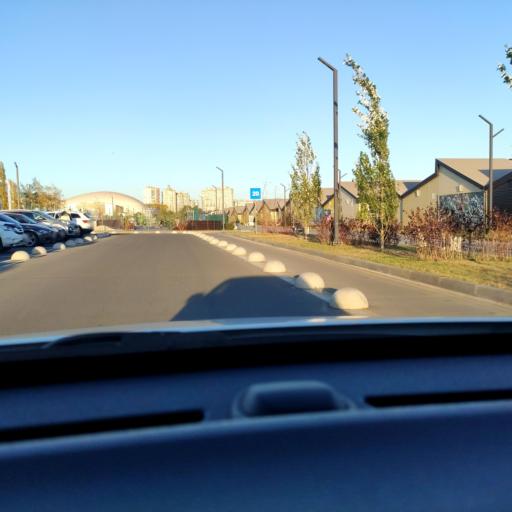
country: RU
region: Voronezj
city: Voronezh
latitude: 51.6708
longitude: 39.2315
